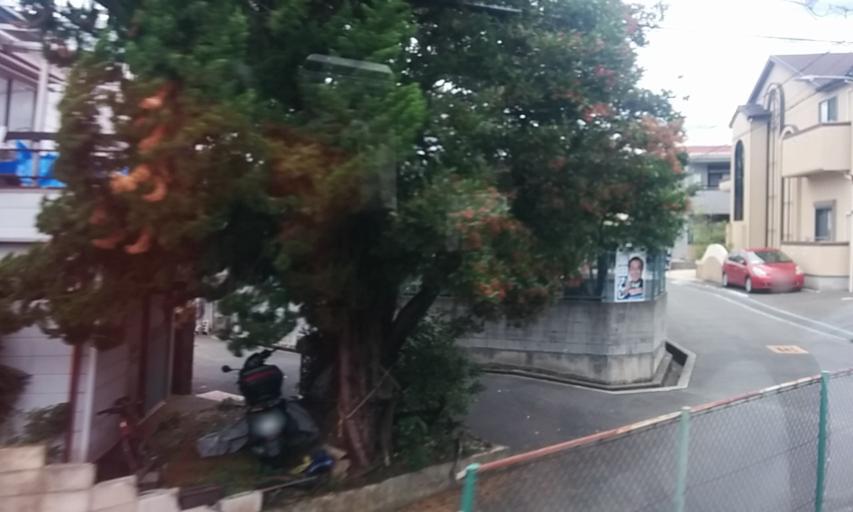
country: JP
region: Osaka
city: Ikeda
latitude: 34.8116
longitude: 135.4506
